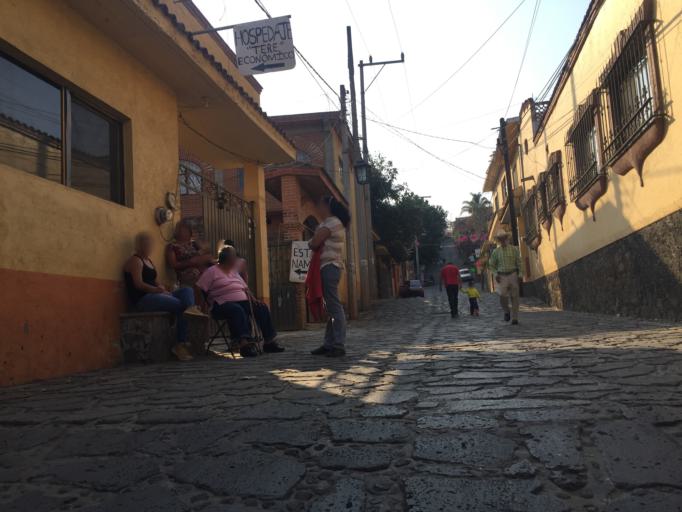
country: MX
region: Morelos
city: Tepoztlan
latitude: 18.9827
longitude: -99.1033
